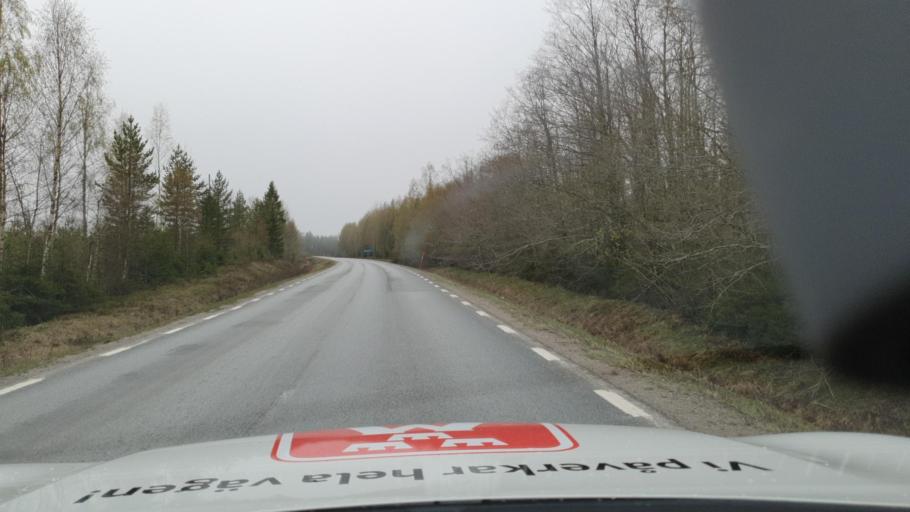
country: SE
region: Vaesterbotten
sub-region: Vannas Kommun
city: Vaennaes
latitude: 63.7771
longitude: 19.7291
